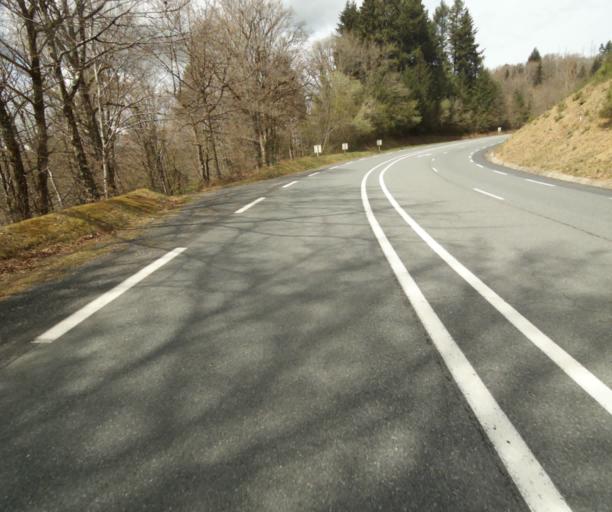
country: FR
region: Limousin
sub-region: Departement de la Correze
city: Sainte-Fortunade
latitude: 45.1926
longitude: 1.8403
